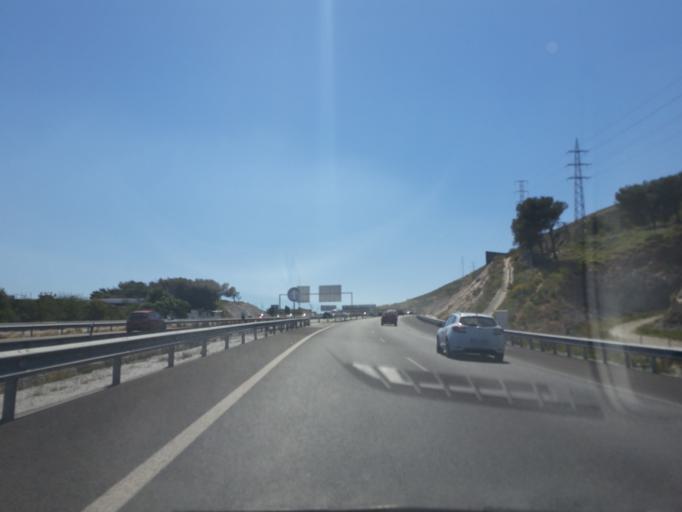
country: ES
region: Andalusia
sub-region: Provincia de Malaga
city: Torremolinos
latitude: 36.6279
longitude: -4.5147
